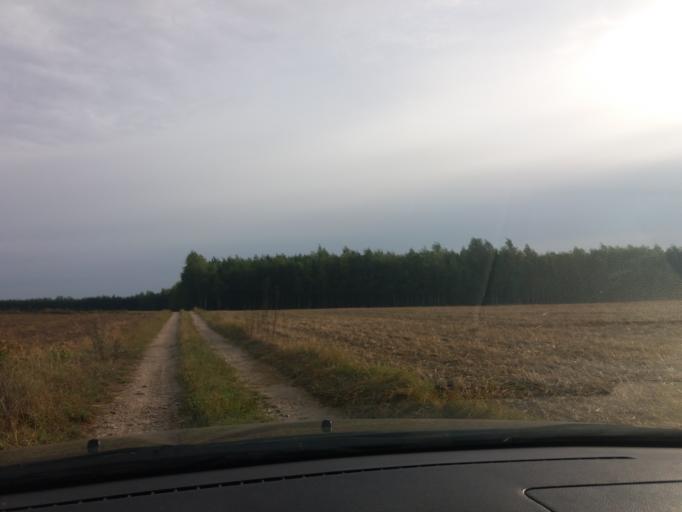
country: PL
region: Masovian Voivodeship
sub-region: Powiat mlawski
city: Wieczfnia Koscielna
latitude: 53.2142
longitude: 20.4554
